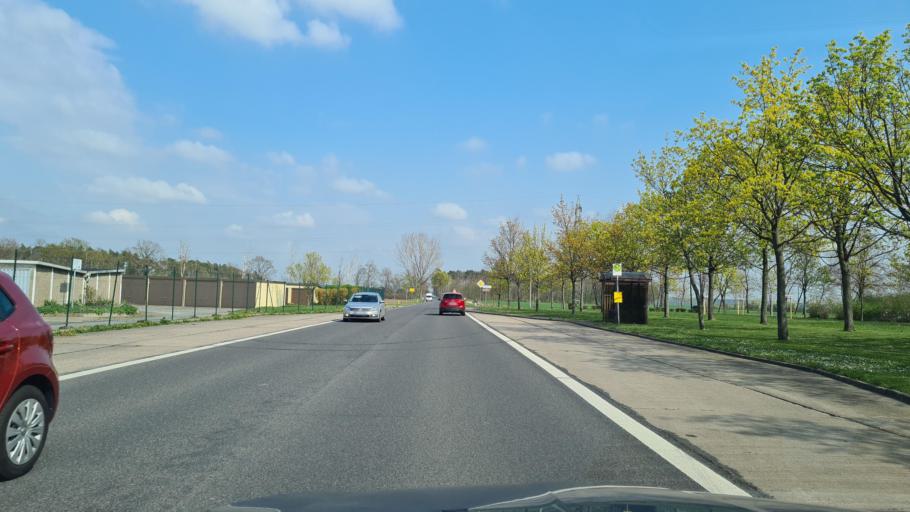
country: DE
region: Saxony
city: Nauwalde
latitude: 51.4135
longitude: 13.4592
